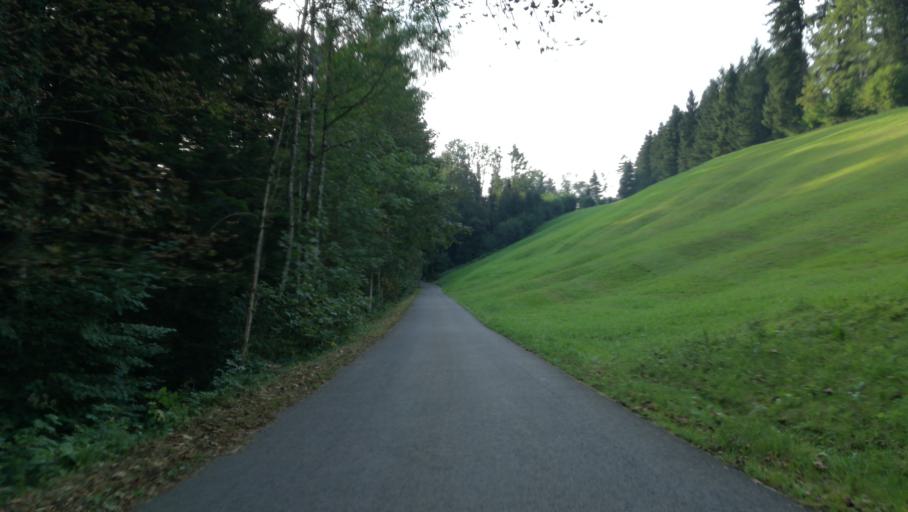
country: CH
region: Zug
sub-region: Zug
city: Unterageri
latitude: 47.1514
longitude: 8.5602
